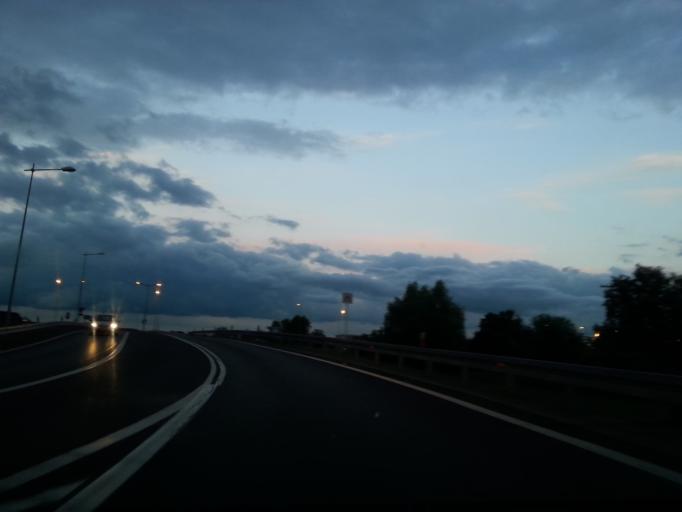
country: PL
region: Lower Silesian Voivodeship
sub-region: Powiat wroclawski
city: Bielany Wroclawskie
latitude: 51.0493
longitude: 16.9697
